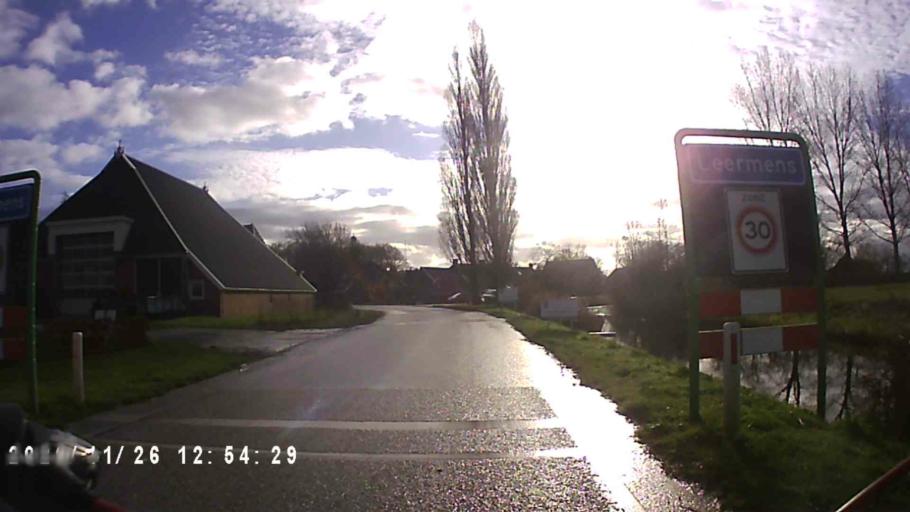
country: NL
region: Groningen
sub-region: Gemeente Appingedam
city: Appingedam
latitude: 53.3478
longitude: 6.7949
